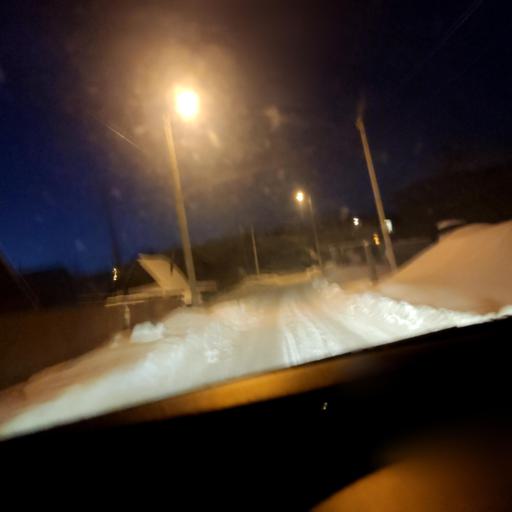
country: RU
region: Perm
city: Froly
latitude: 57.9495
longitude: 56.3057
